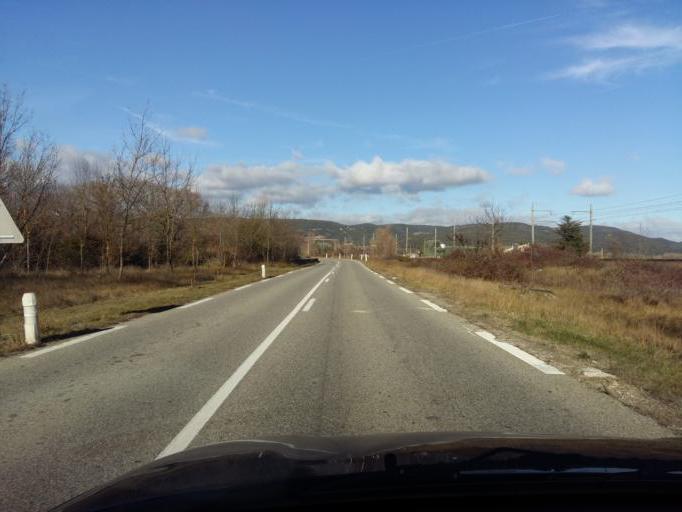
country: FR
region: Rhone-Alpes
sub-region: Departement de l'Ardeche
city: Bourg-Saint-Andeol
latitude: 44.4168
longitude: 4.6542
